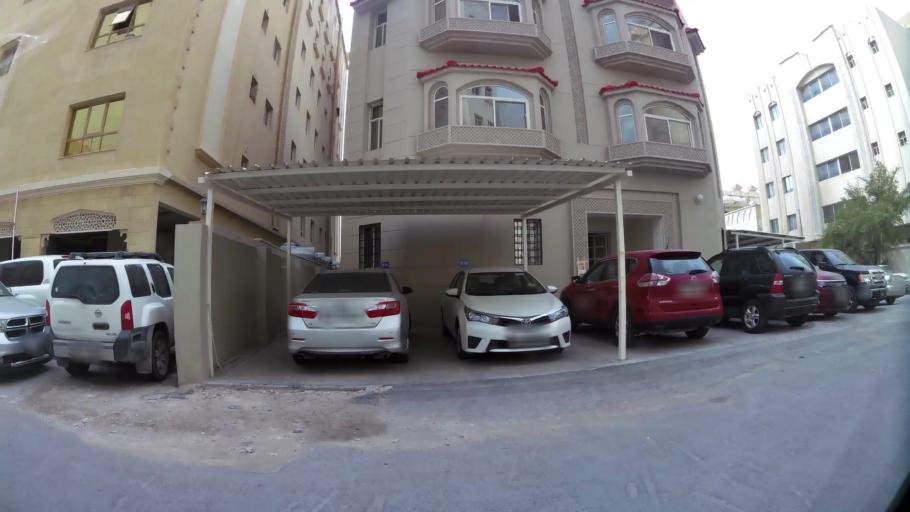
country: QA
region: Baladiyat ad Dawhah
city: Doha
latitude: 25.2887
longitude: 51.4975
